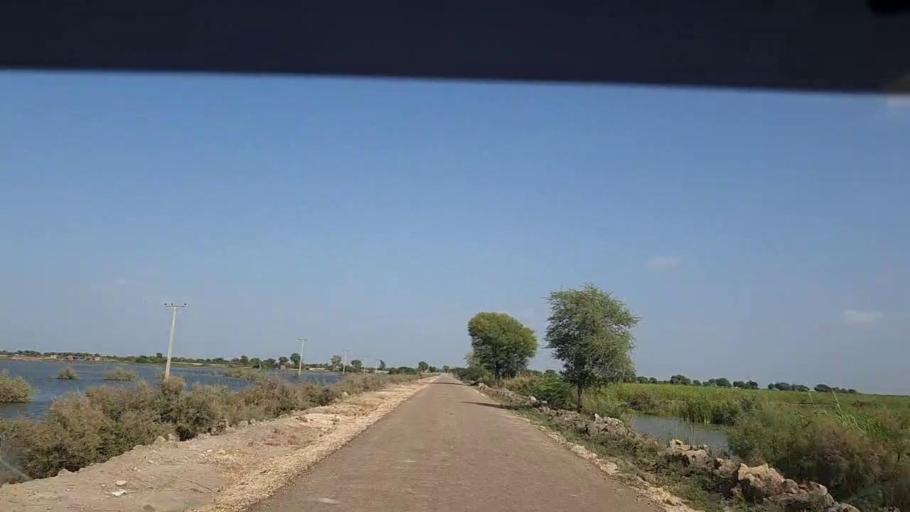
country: PK
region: Sindh
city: Kadhan
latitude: 24.4645
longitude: 68.8421
